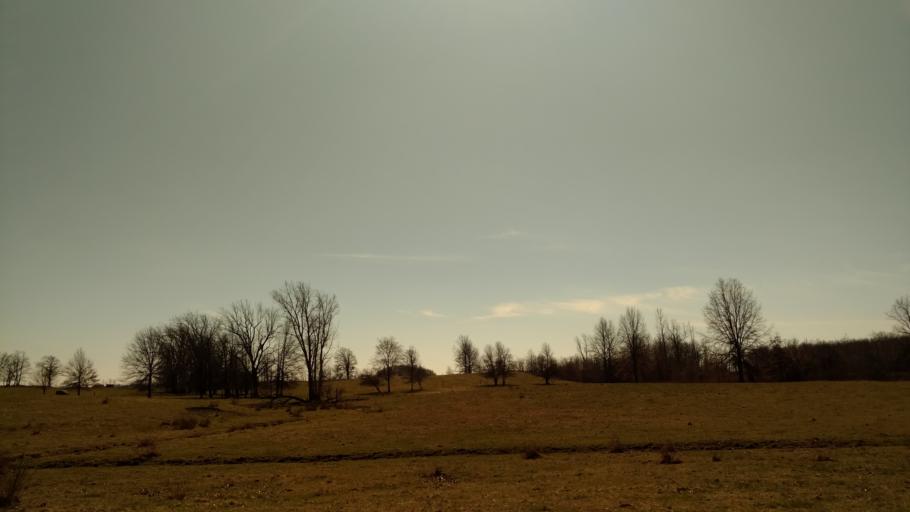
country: US
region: Ohio
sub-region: Union County
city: Richwood
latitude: 40.5127
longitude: -83.3489
